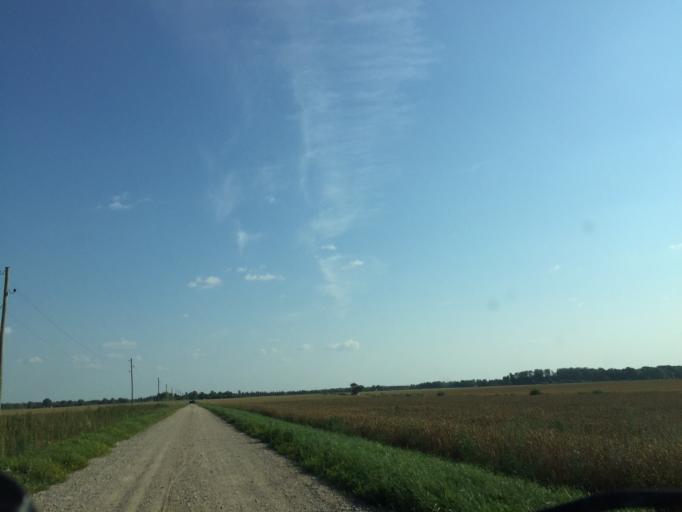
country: LV
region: Jelgava
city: Jelgava
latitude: 56.4650
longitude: 23.6803
